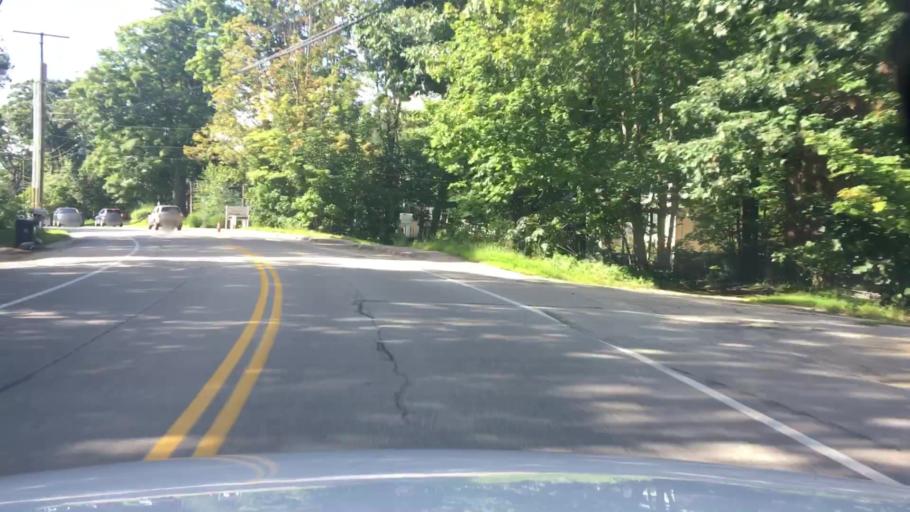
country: US
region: New Hampshire
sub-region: Strafford County
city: Dover
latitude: 43.1739
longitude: -70.8737
